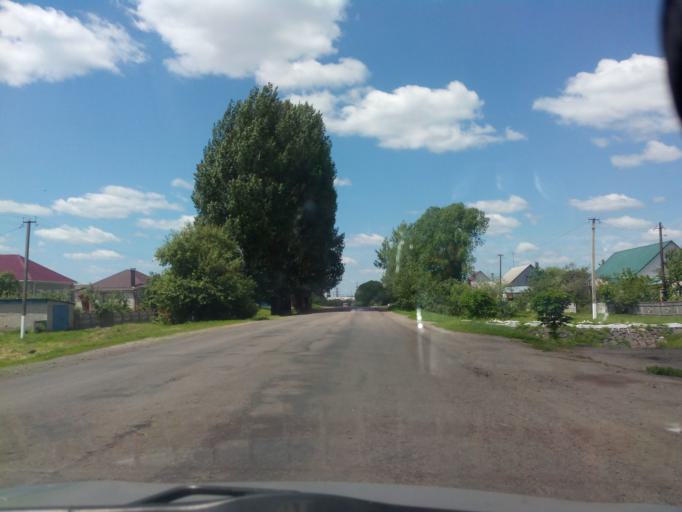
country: RU
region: Voronezj
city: Ternovka
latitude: 51.6756
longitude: 41.6110
